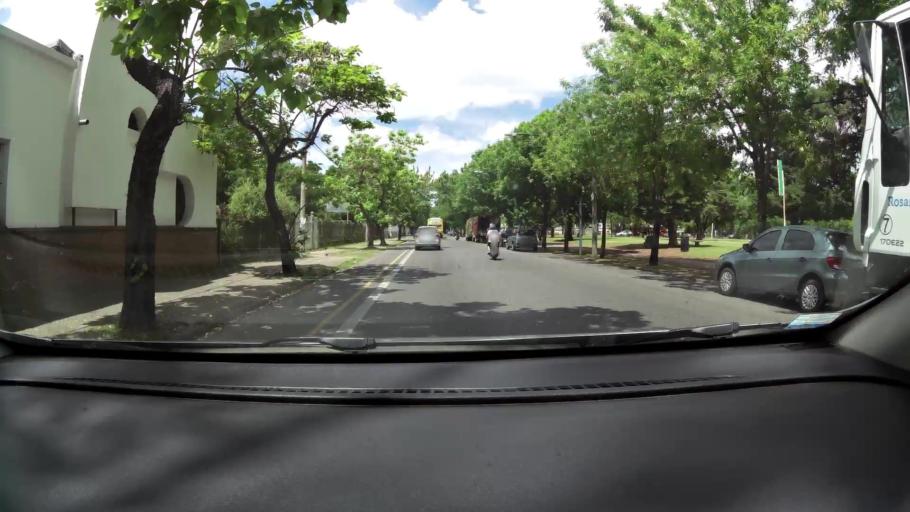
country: AR
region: Santa Fe
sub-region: Departamento de Rosario
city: Rosario
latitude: -32.9709
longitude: -60.6340
